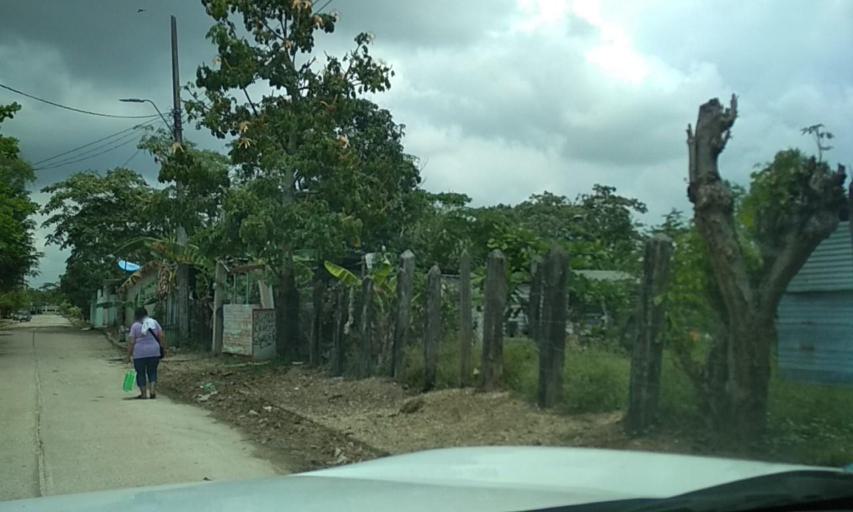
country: MX
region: Veracruz
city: Las Choapas
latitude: 17.8923
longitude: -94.0971
